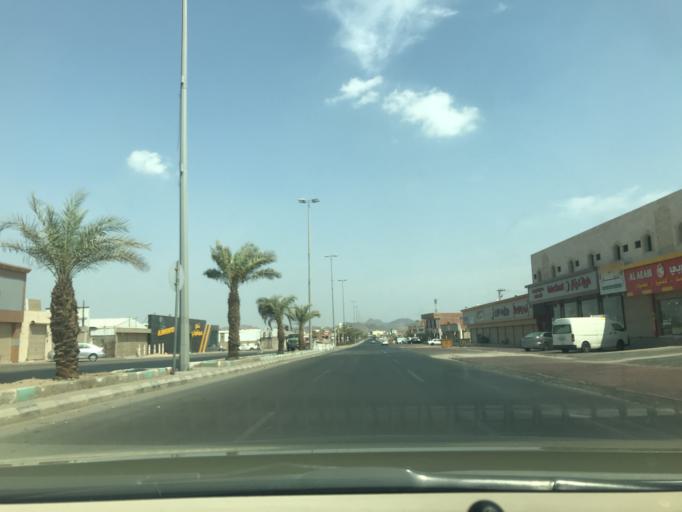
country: SA
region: Makkah
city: Al Jumum
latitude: 21.6229
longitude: 39.6827
